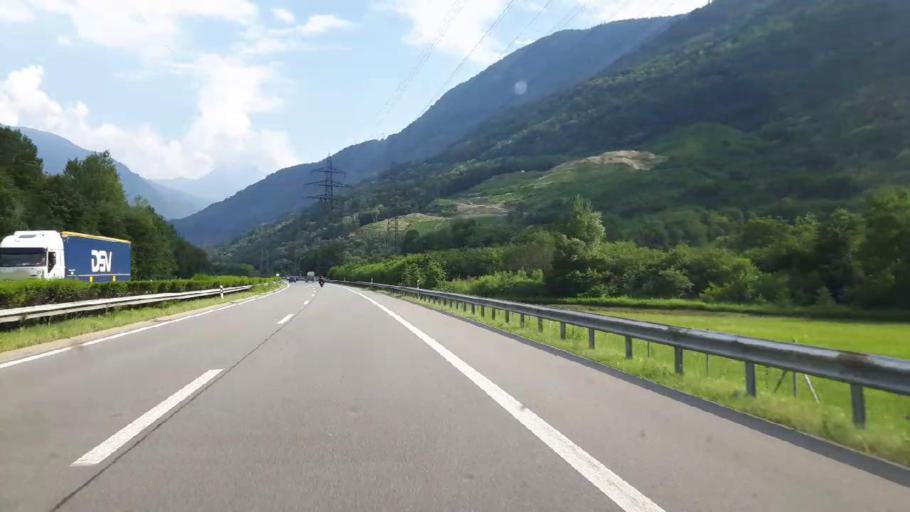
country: CH
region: Ticino
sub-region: Riviera District
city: Claro
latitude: 46.2533
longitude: 9.0096
